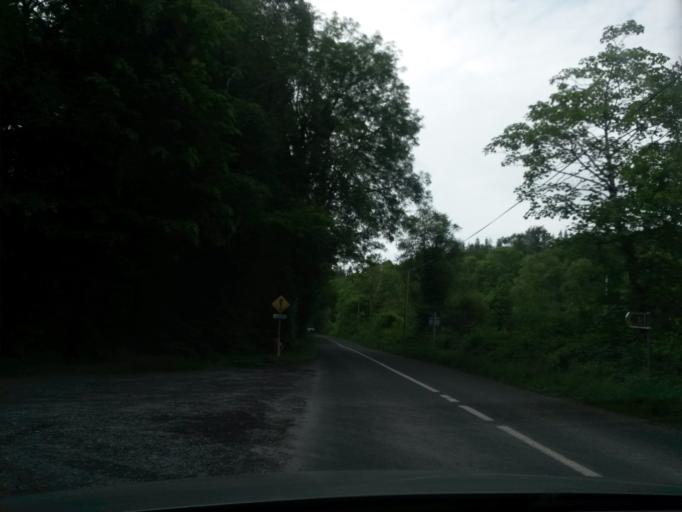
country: IE
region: Connaught
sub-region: Sligo
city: Sligo
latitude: 54.2313
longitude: -8.4026
